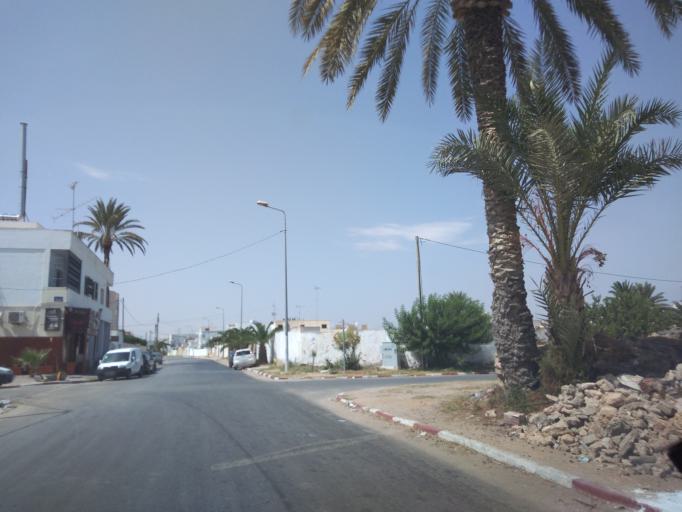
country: TN
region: Safaqis
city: Sfax
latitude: 34.7562
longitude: 10.7529
